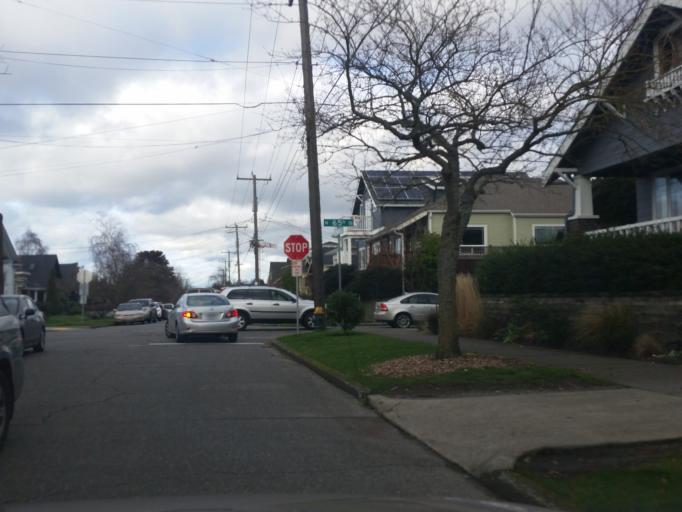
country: US
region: Washington
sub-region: King County
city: Seattle
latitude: 47.6759
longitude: -122.3552
